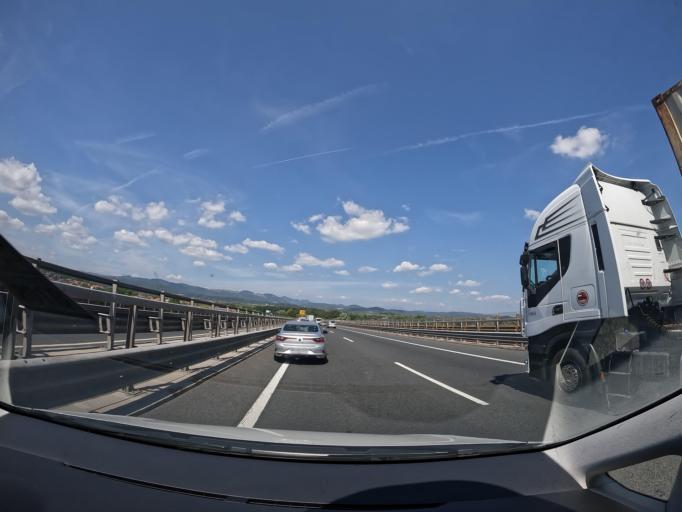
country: SI
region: Vrhnika
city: Verd
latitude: 45.9568
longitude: 14.3123
